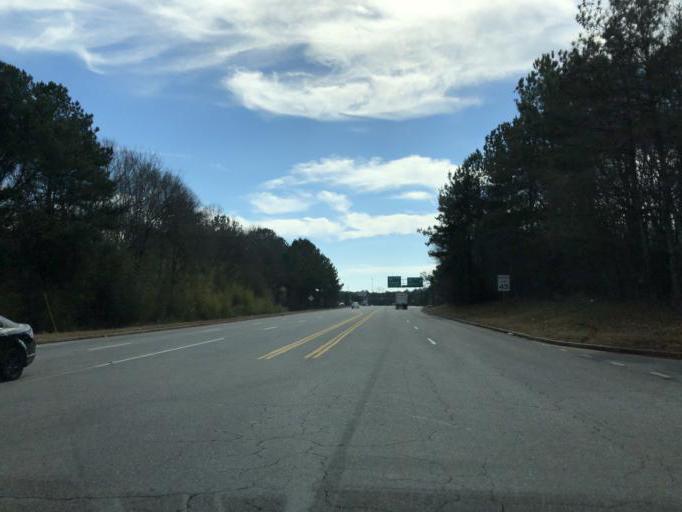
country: US
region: South Carolina
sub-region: Spartanburg County
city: Mayo
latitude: 35.0304
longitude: -81.8776
